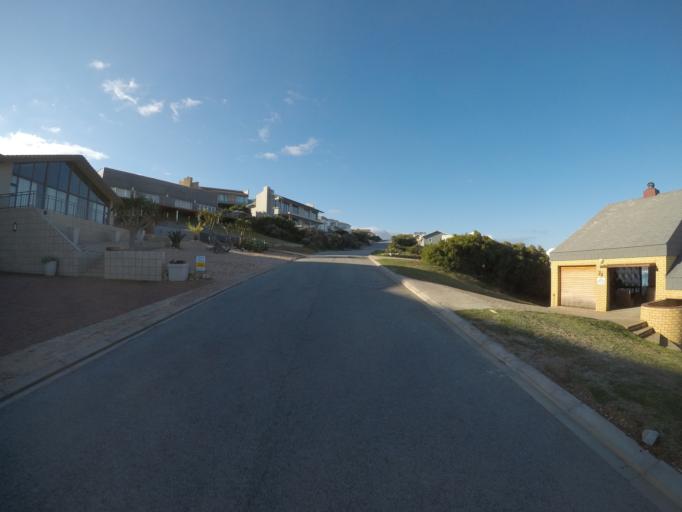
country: ZA
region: Western Cape
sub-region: Eden District Municipality
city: Riversdale
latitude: -34.4218
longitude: 21.3456
